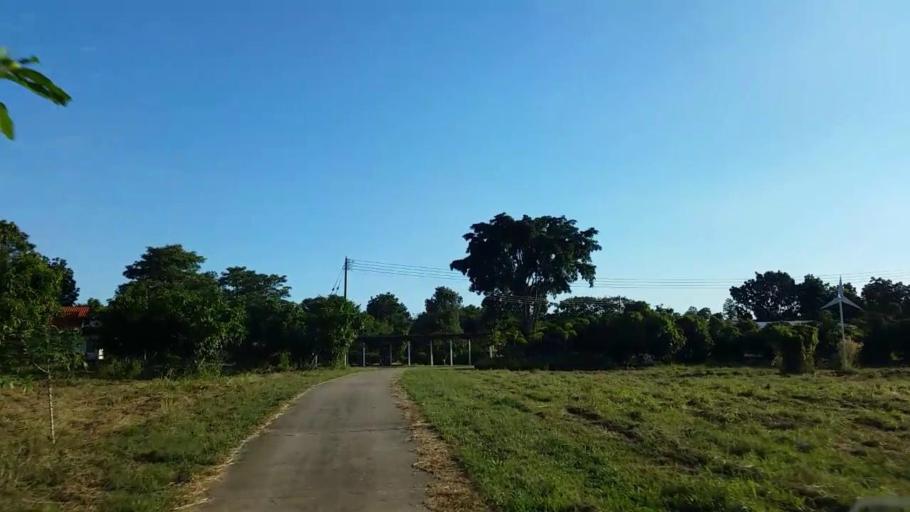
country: TH
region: Chaiyaphum
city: Thep Sathit
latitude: 15.5510
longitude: 101.4760
